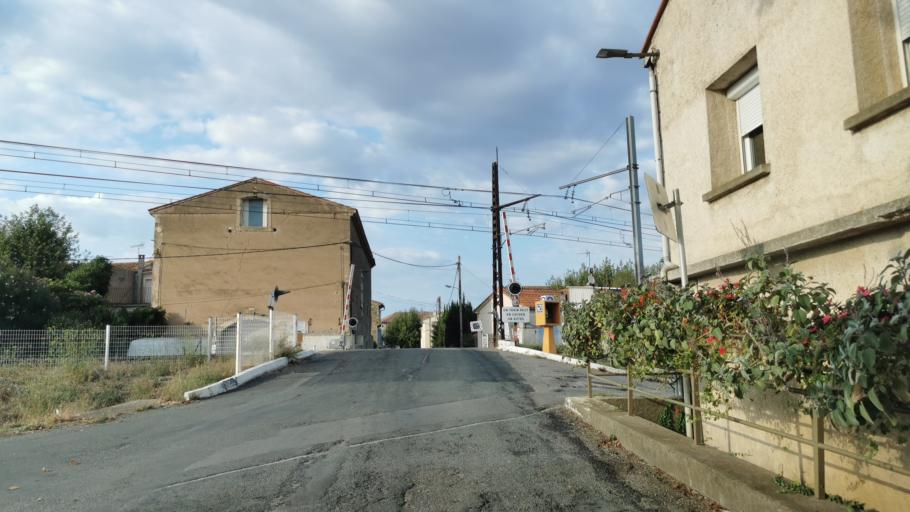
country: FR
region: Languedoc-Roussillon
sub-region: Departement de l'Aude
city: Nevian
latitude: 43.2098
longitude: 2.9039
